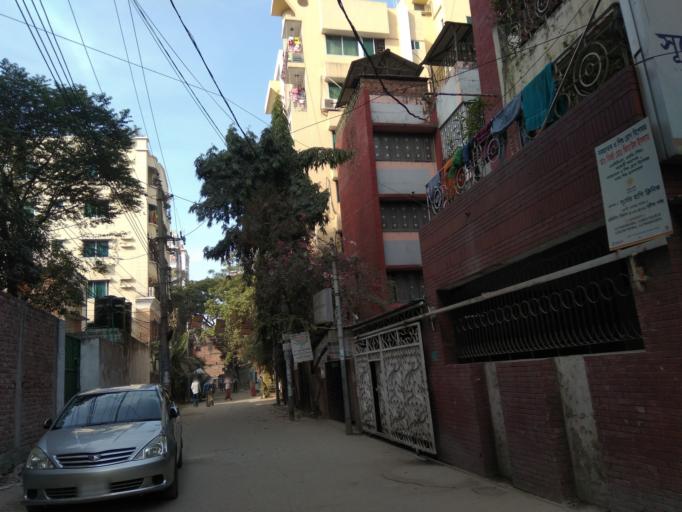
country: BD
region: Dhaka
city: Azimpur
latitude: 23.7718
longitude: 90.3580
